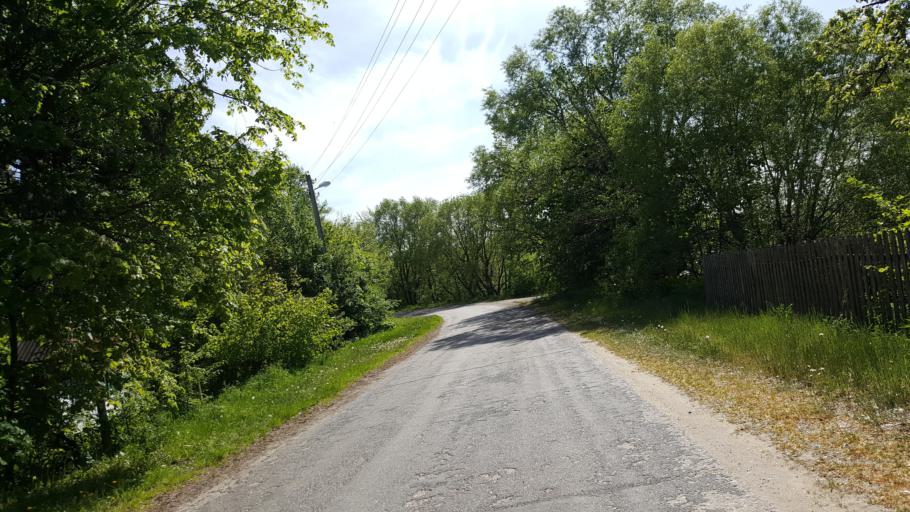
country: BY
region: Brest
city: Zhabinka
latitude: 52.3258
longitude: 24.0841
